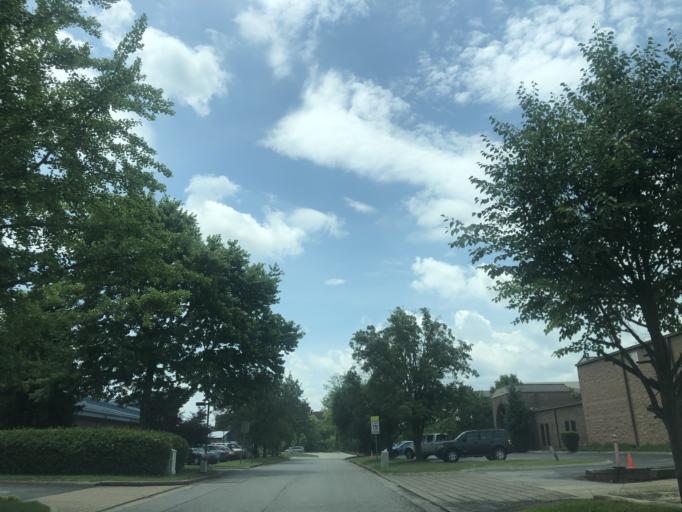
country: US
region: Tennessee
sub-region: Davidson County
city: Nashville
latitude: 36.1955
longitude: -86.7955
